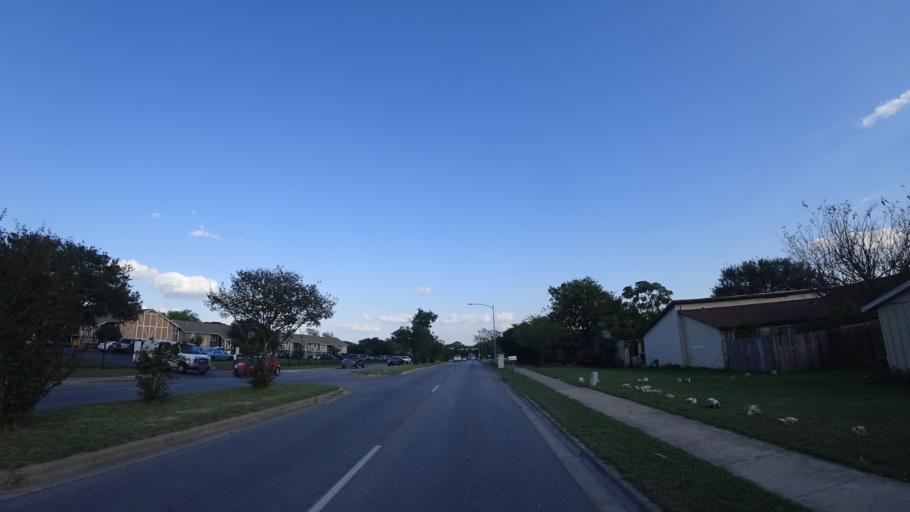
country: US
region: Texas
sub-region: Travis County
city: Wells Branch
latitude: 30.3661
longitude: -97.7034
